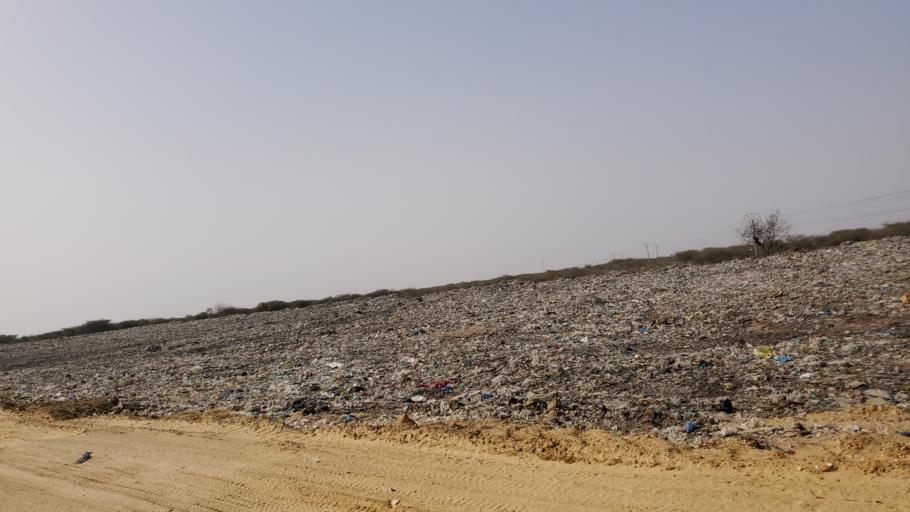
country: SN
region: Saint-Louis
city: Saint-Louis
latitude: 15.9490
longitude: -16.4335
